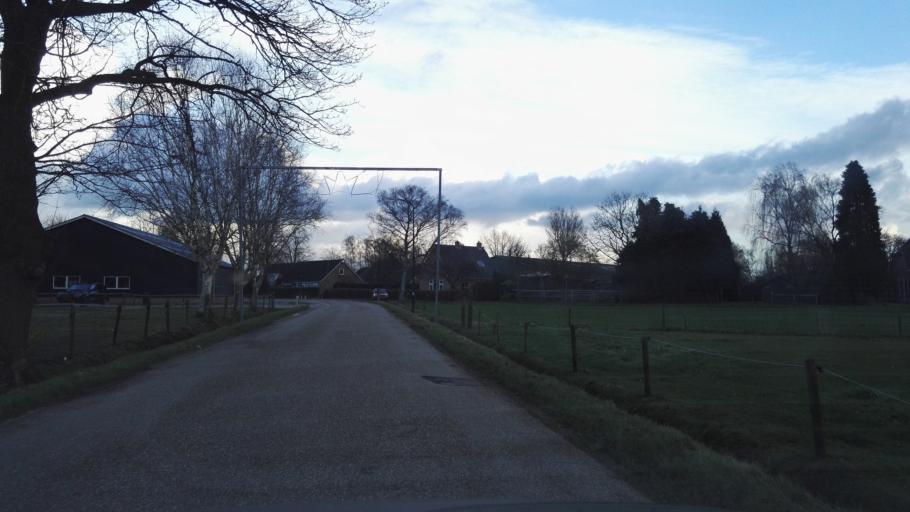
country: NL
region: Gelderland
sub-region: Gemeente Epe
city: Vaassen
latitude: 52.2549
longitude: 5.9886
